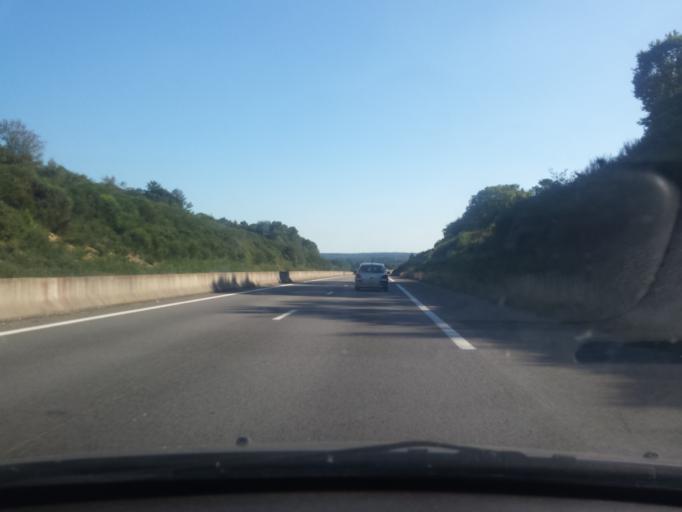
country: FR
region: Brittany
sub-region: Departement du Morbihan
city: Colpo
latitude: 47.7957
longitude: -2.8040
